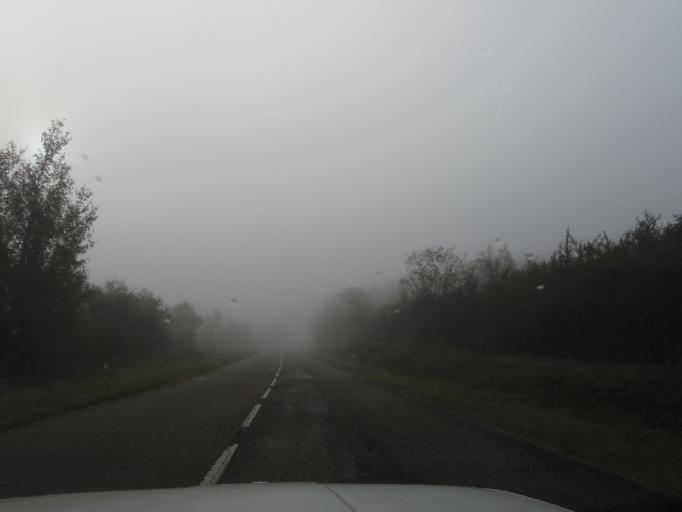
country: FR
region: Rhone-Alpes
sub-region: Departement de l'Isere
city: Creys-Mepieu
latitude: 45.7469
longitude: 5.5067
